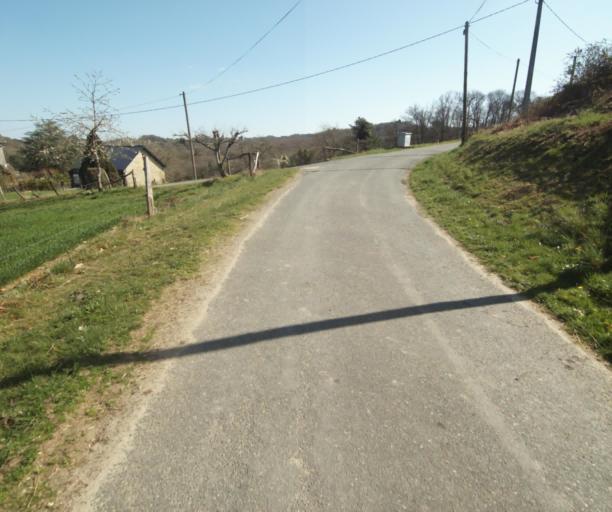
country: FR
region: Limousin
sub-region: Departement de la Correze
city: Saint-Mexant
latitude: 45.2920
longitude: 1.6426
